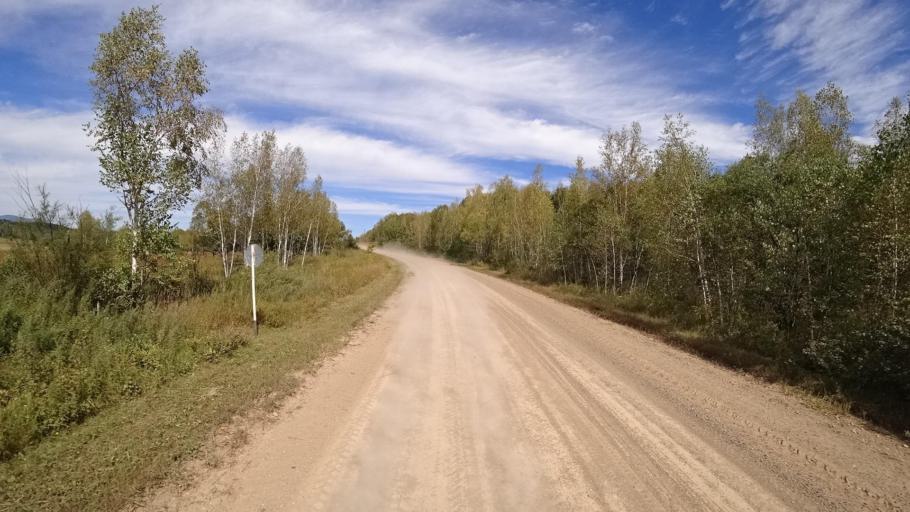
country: RU
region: Primorskiy
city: Yakovlevka
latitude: 44.6803
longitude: 133.6168
